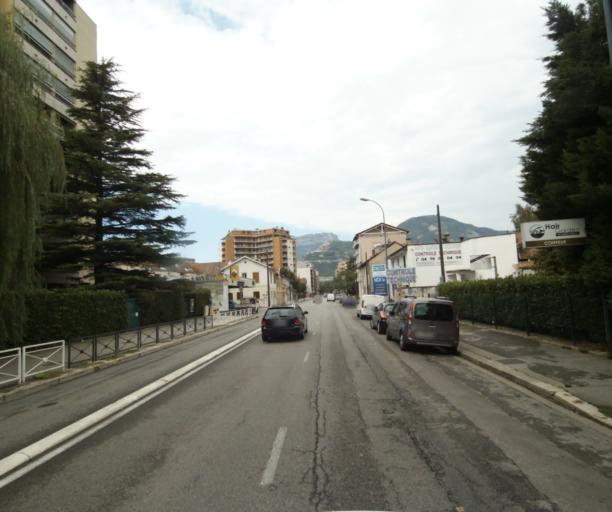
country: FR
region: Rhone-Alpes
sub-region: Departement de l'Isere
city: Grenoble
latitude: 45.1788
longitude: 5.7359
